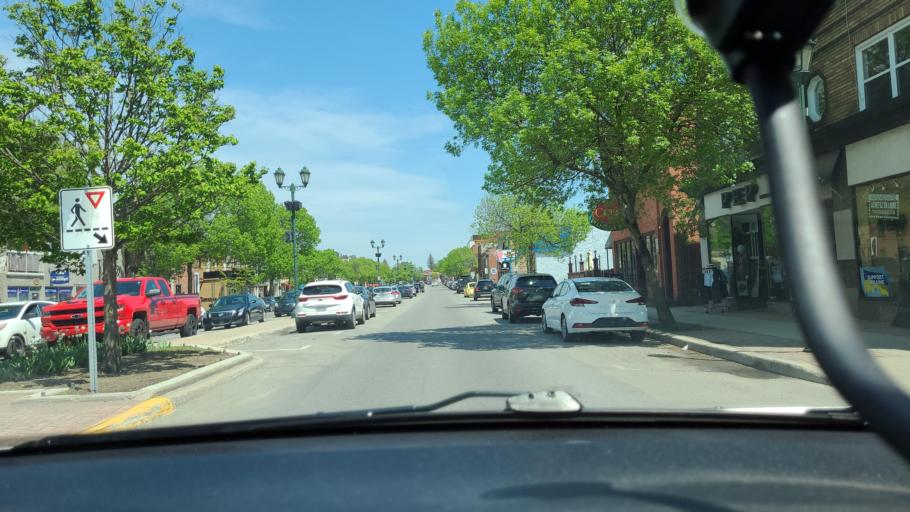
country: CA
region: Quebec
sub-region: Laurentides
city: Lachute
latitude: 45.6566
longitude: -74.3358
